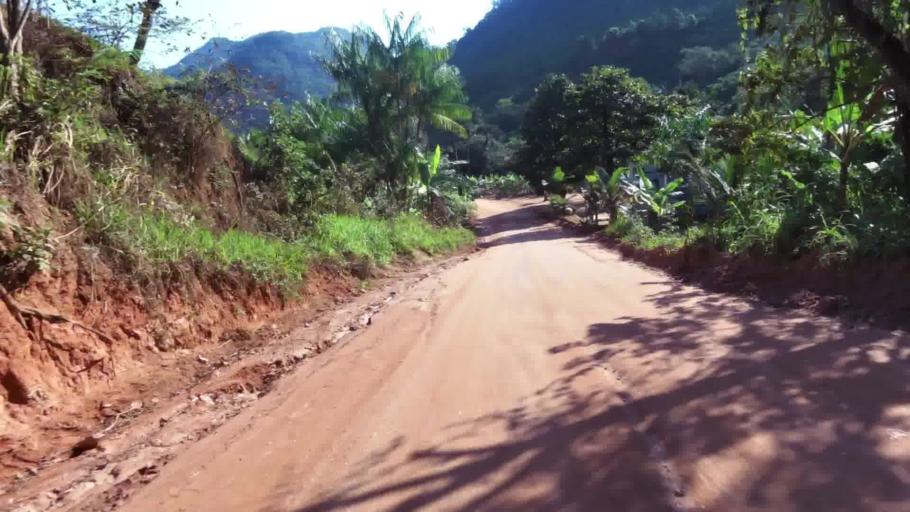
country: BR
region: Espirito Santo
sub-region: Alfredo Chaves
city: Alfredo Chaves
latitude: -20.6130
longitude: -40.7758
